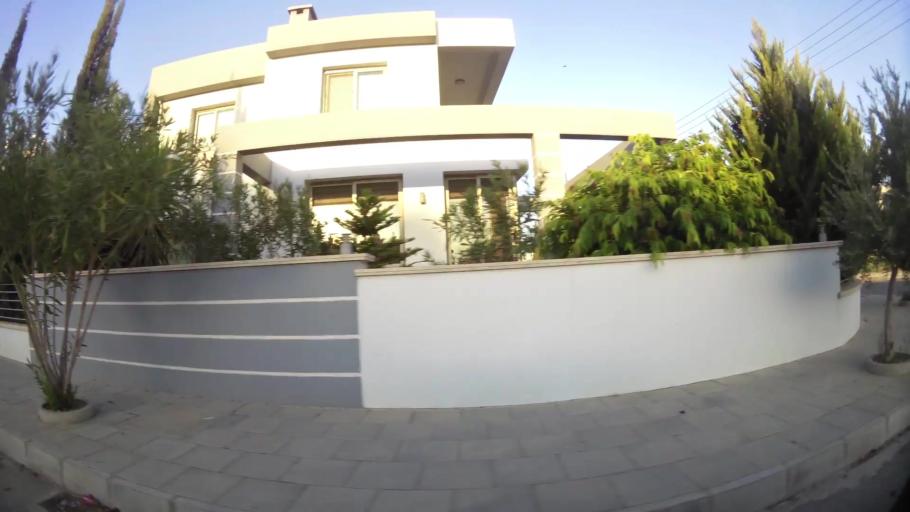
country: CY
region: Lefkosia
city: Nicosia
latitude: 35.1894
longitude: 33.3224
